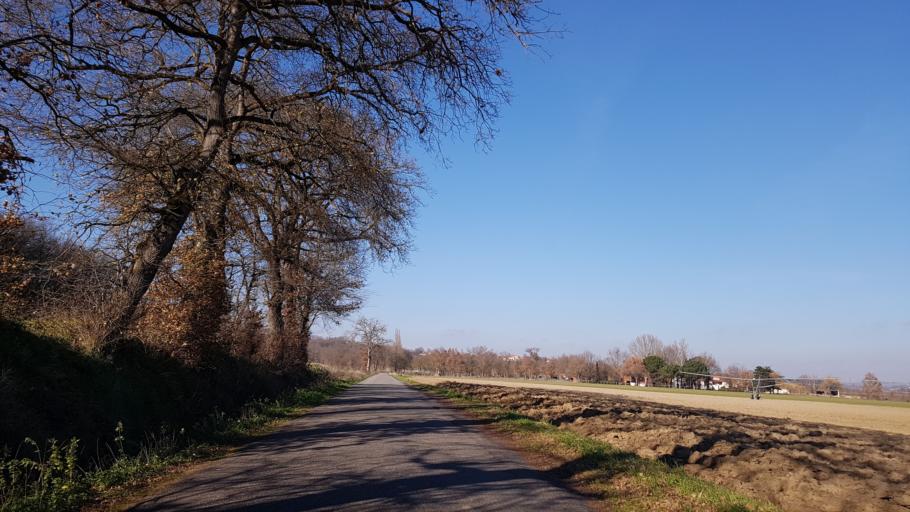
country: FR
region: Midi-Pyrenees
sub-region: Departement de l'Ariege
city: La Tour-du-Crieu
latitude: 43.1274
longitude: 1.7190
